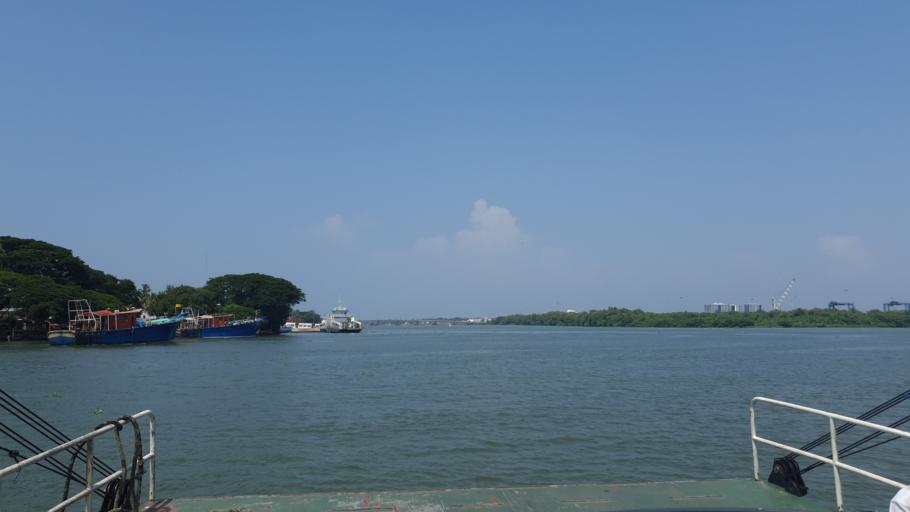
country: IN
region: Kerala
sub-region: Ernakulam
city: Cochin
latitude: 9.9714
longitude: 76.2450
